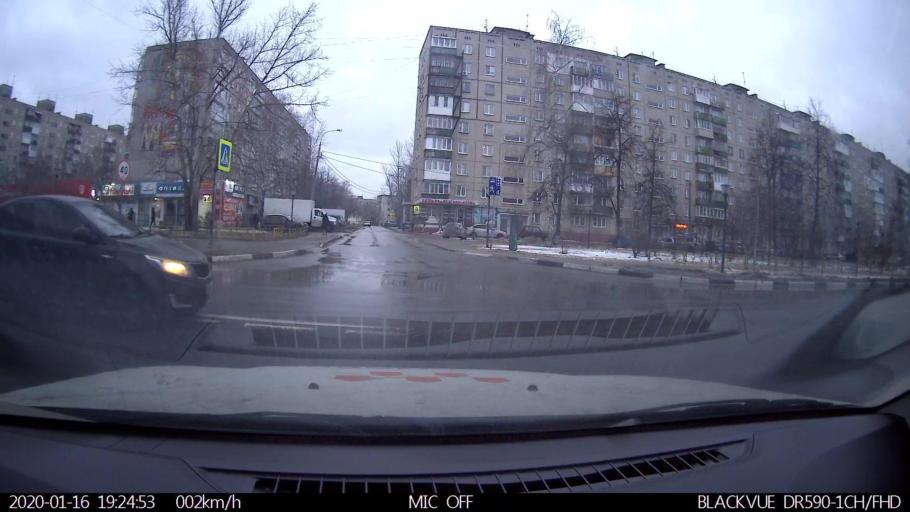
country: RU
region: Nizjnij Novgorod
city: Gorbatovka
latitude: 56.3649
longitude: 43.8213
